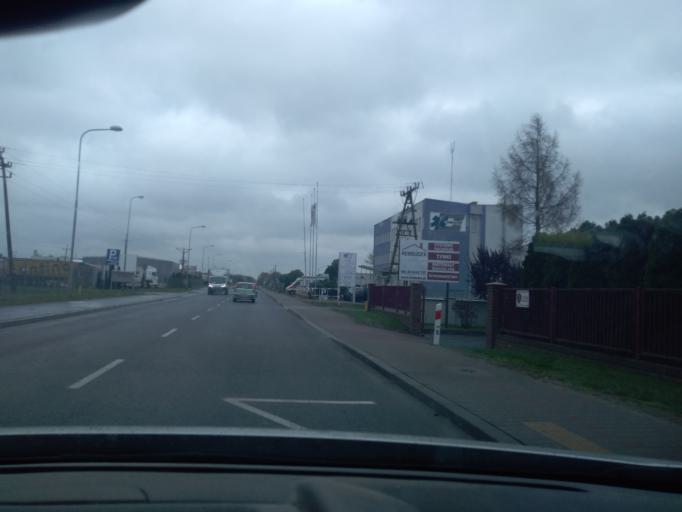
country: PL
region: Greater Poland Voivodeship
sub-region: Powiat obornicki
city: Oborniki
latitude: 52.6441
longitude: 16.8252
